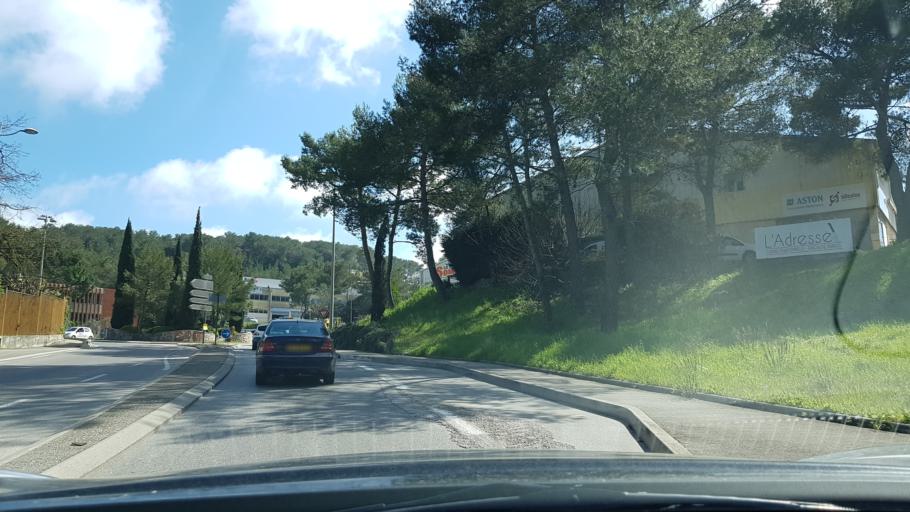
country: FR
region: Provence-Alpes-Cote d'Azur
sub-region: Departement des Alpes-Maritimes
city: Vallauris
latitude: 43.5956
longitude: 7.0574
